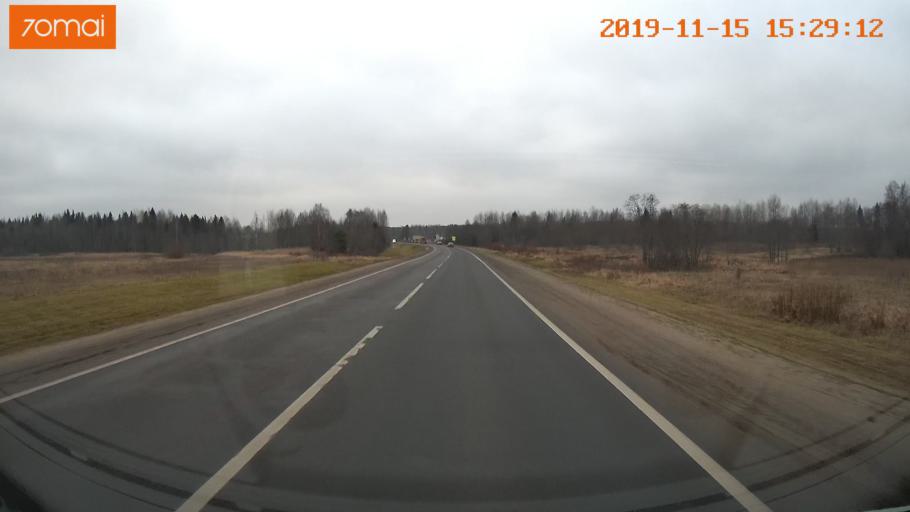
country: RU
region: Jaroslavl
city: Danilov
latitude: 58.1234
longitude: 40.1233
